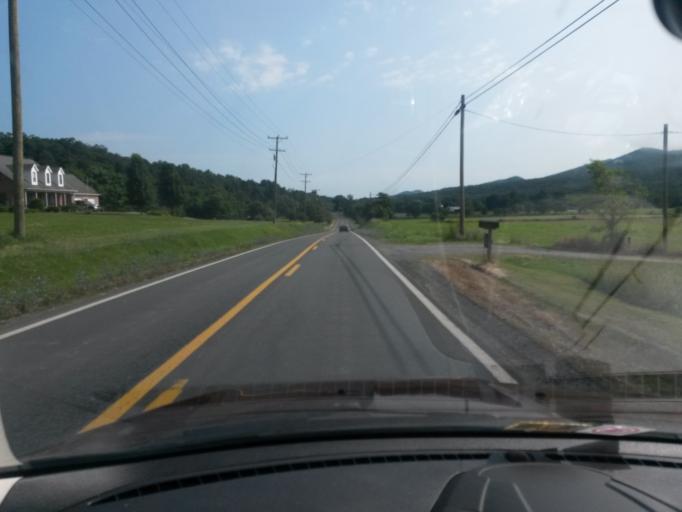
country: US
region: Virginia
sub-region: Shenandoah County
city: Basye
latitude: 38.8940
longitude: -78.8554
